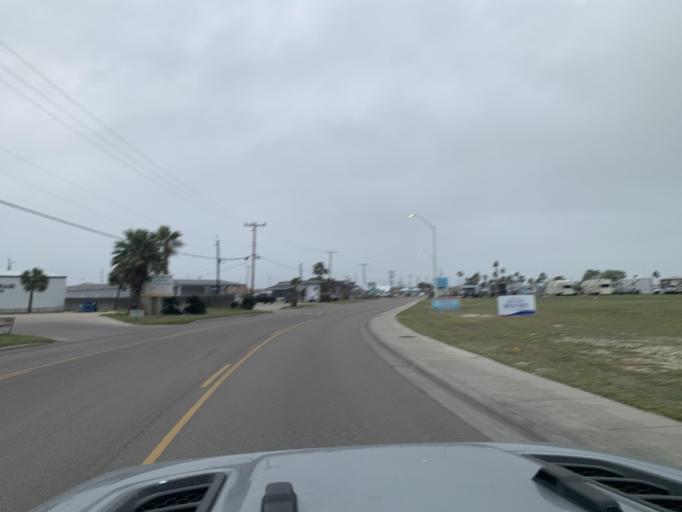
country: US
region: Texas
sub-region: Nueces County
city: Port Aransas
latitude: 27.8317
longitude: -97.0713
